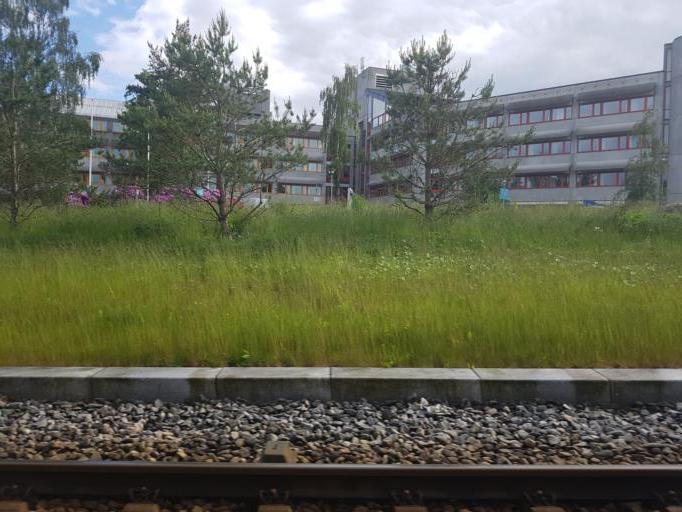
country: NO
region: Hordaland
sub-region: Bergen
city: Ytrebygda
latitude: 60.2978
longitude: 5.2776
